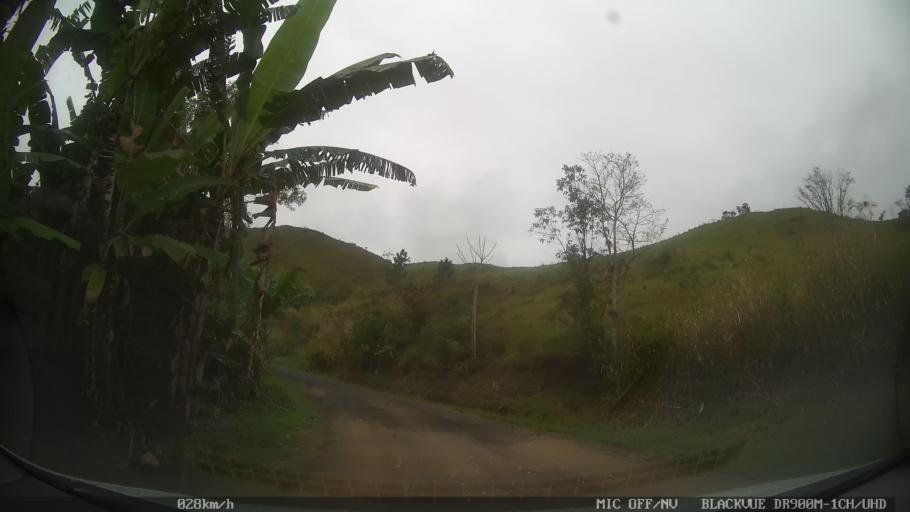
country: BR
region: Sao Paulo
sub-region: Cajati
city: Cajati
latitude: -24.7900
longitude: -48.1816
